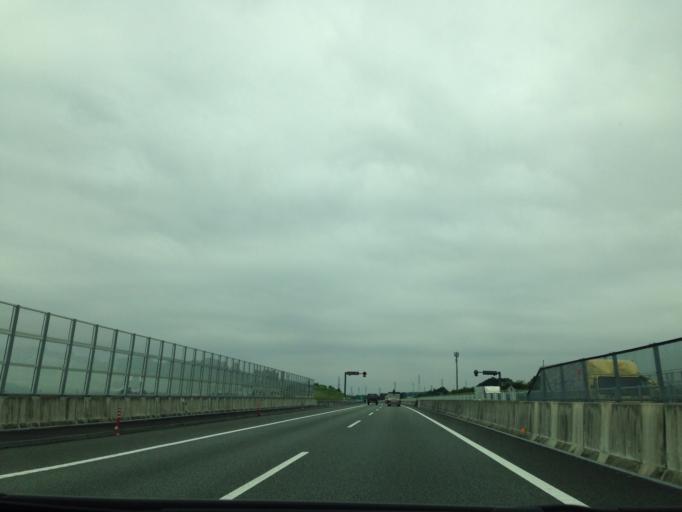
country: JP
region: Shizuoka
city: Fuji
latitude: 35.1853
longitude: 138.7241
